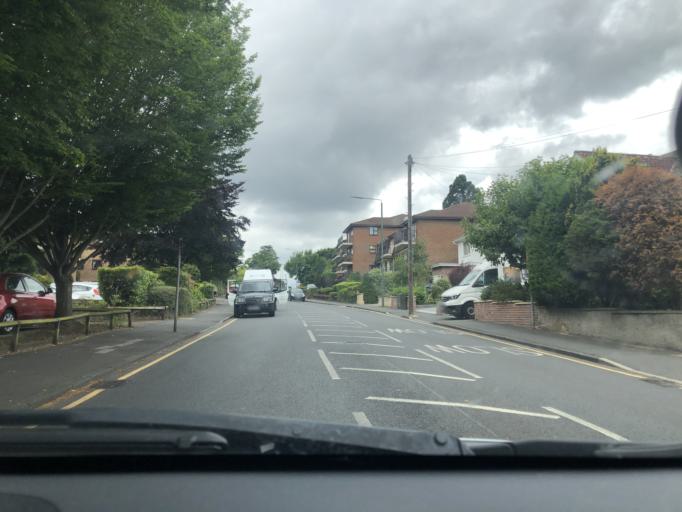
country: GB
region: England
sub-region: Greater London
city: Bexley
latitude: 51.4428
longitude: 0.1428
